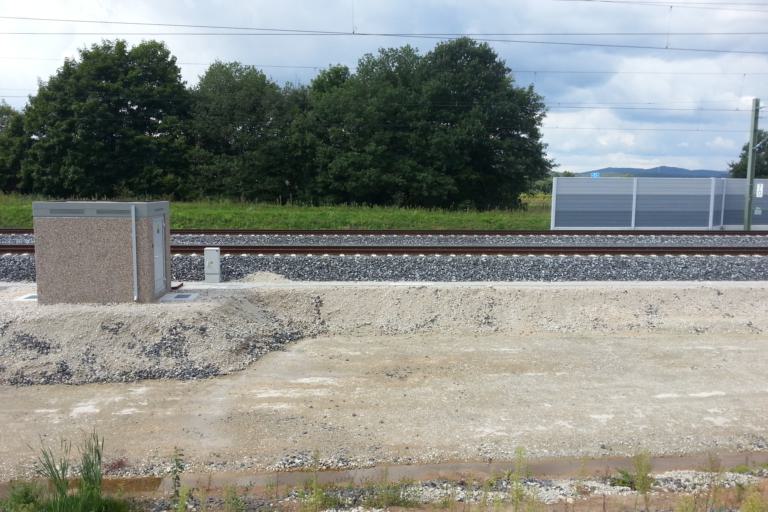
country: DE
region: Bavaria
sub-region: Upper Franconia
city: Kemmern
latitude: 49.9608
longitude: 10.8869
